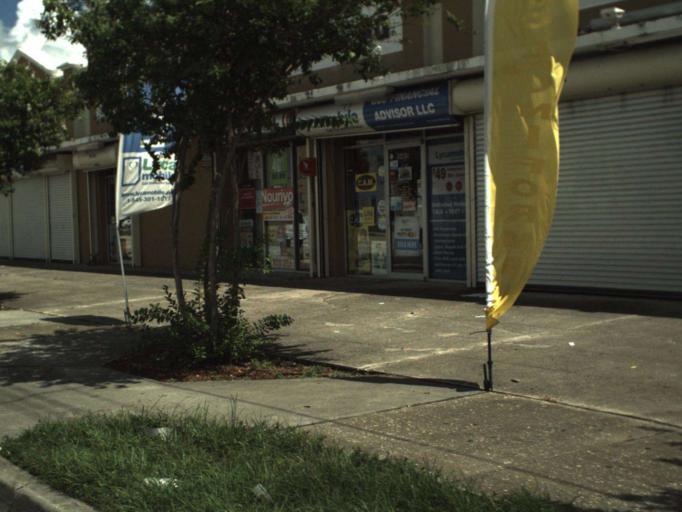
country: US
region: Florida
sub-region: Miami-Dade County
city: Pinewood
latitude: 25.8707
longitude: -80.2099
